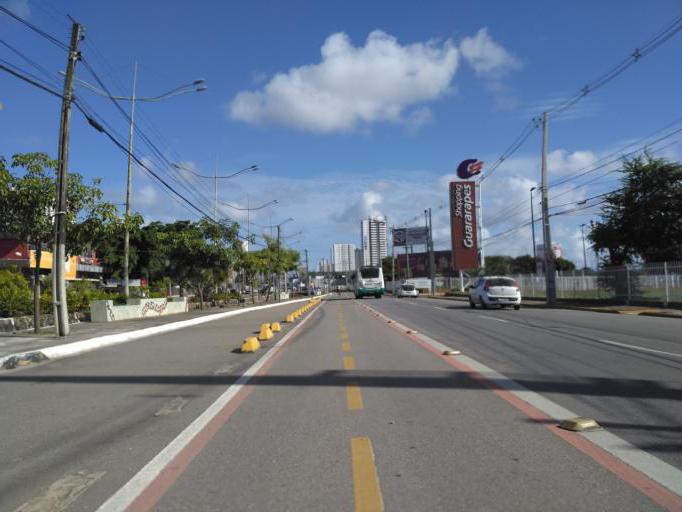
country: BR
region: Pernambuco
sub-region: Jaboatao Dos Guararapes
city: Jaboatao
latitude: -8.1667
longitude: -34.9162
